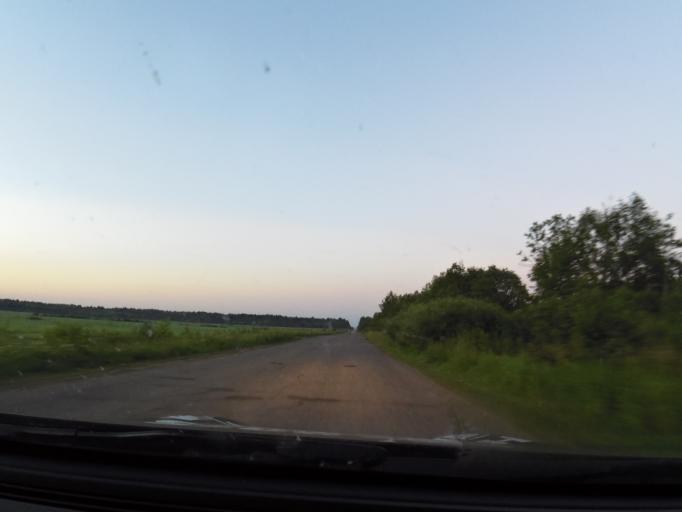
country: RU
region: Kostroma
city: Buy
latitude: 58.4809
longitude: 41.4559
